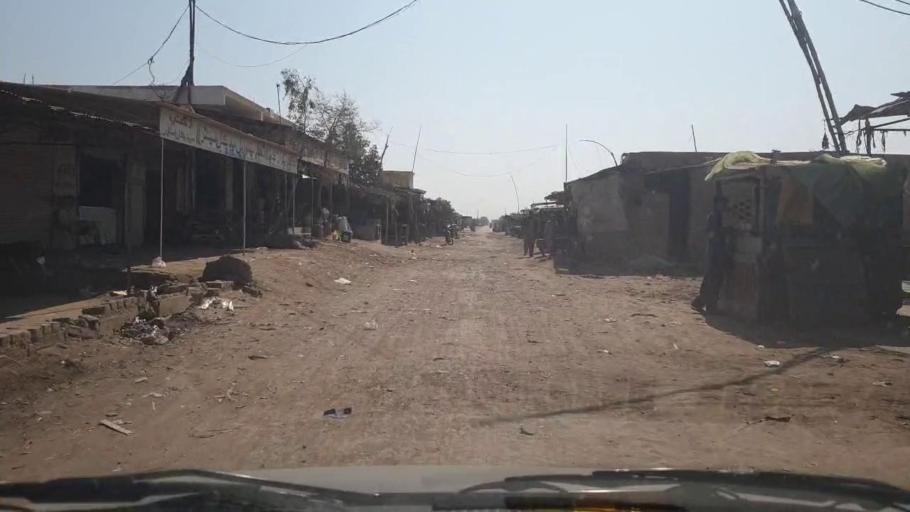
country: PK
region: Sindh
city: Samaro
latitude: 25.2771
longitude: 69.3413
